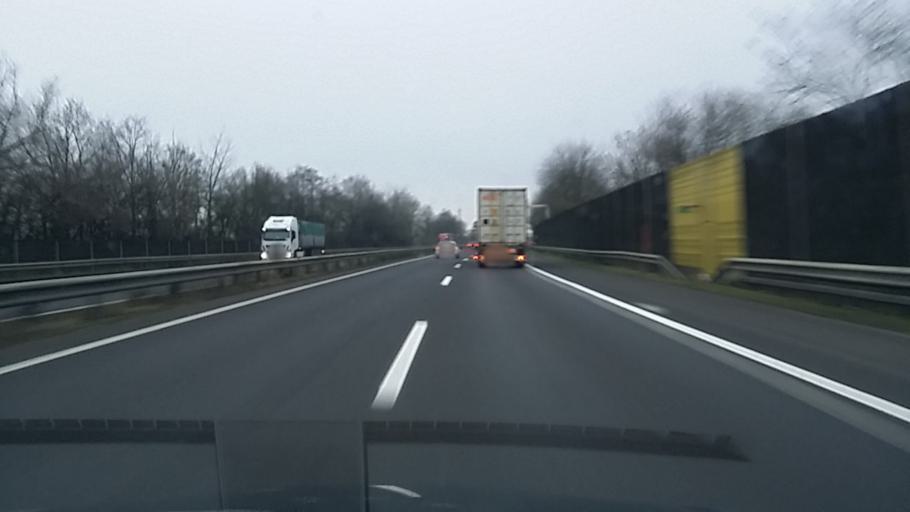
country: AT
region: Upper Austria
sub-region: Wels Stadt
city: Wels
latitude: 48.1904
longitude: 14.0372
